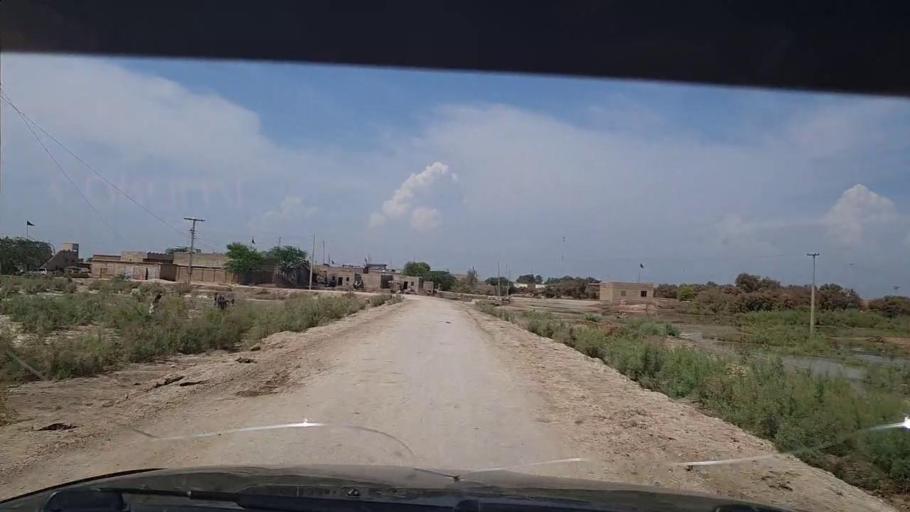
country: PK
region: Sindh
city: Tangwani
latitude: 28.2633
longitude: 69.0001
